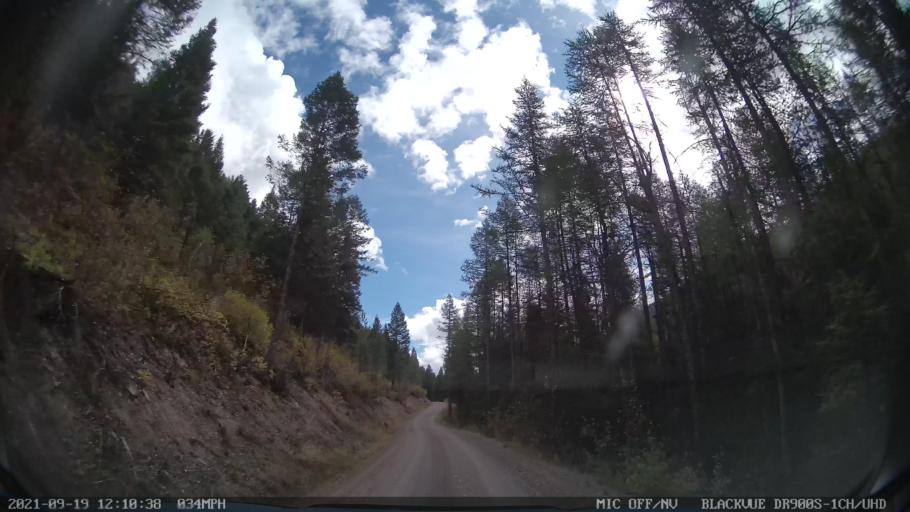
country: US
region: Montana
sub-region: Missoula County
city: Seeley Lake
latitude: 47.1778
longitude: -113.3815
